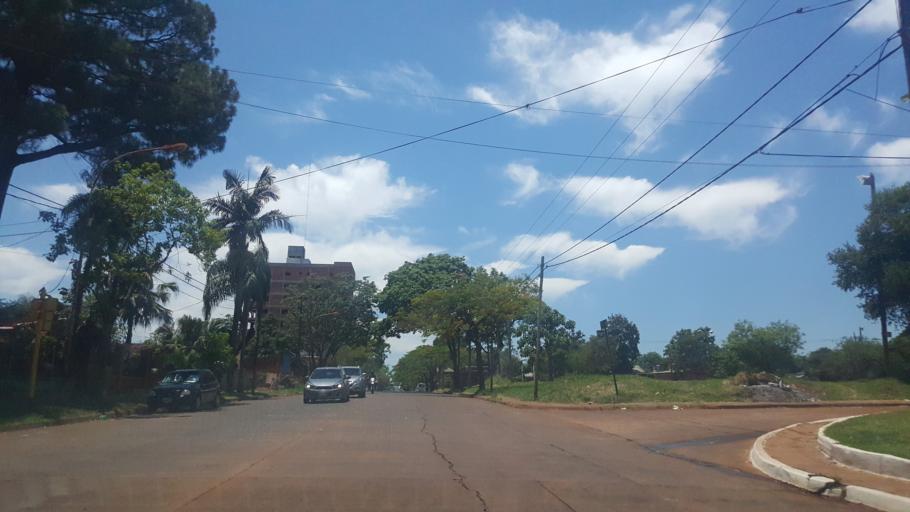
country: AR
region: Misiones
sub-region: Departamento de Capital
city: Posadas
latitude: -27.3682
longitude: -55.9236
